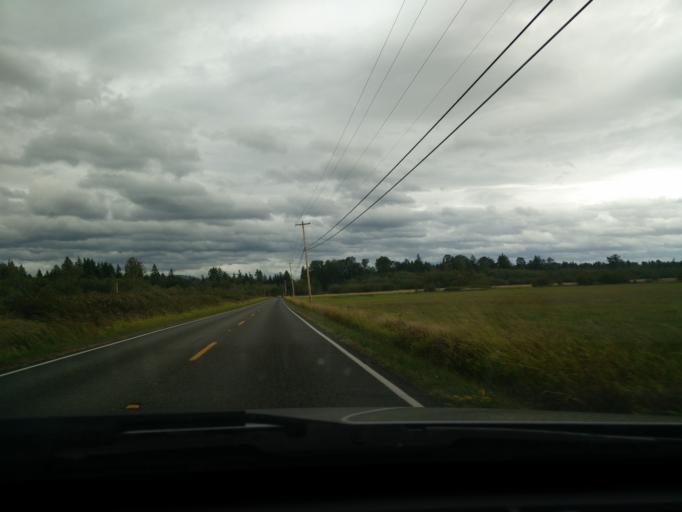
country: US
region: Washington
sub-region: Snohomish County
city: Stanwood
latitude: 48.2687
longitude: -122.3185
